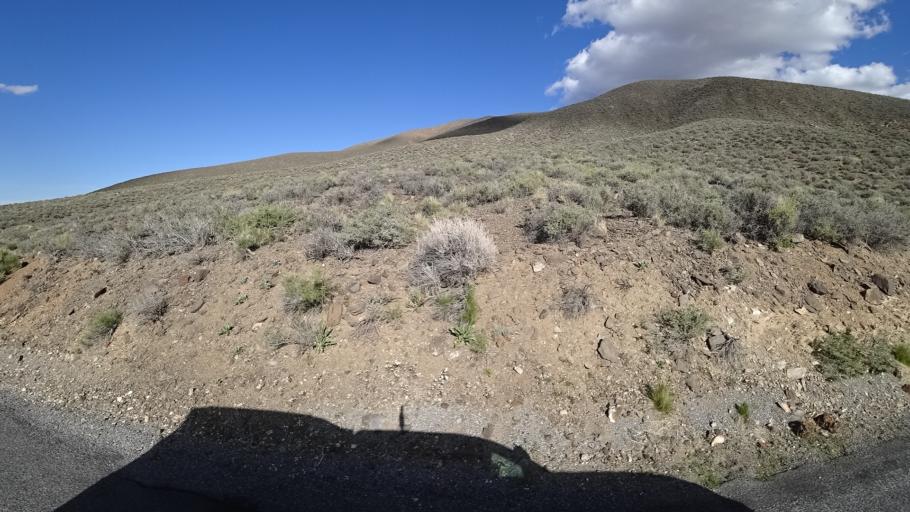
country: US
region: California
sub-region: San Bernardino County
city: Searles Valley
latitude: 36.3248
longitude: -117.1499
